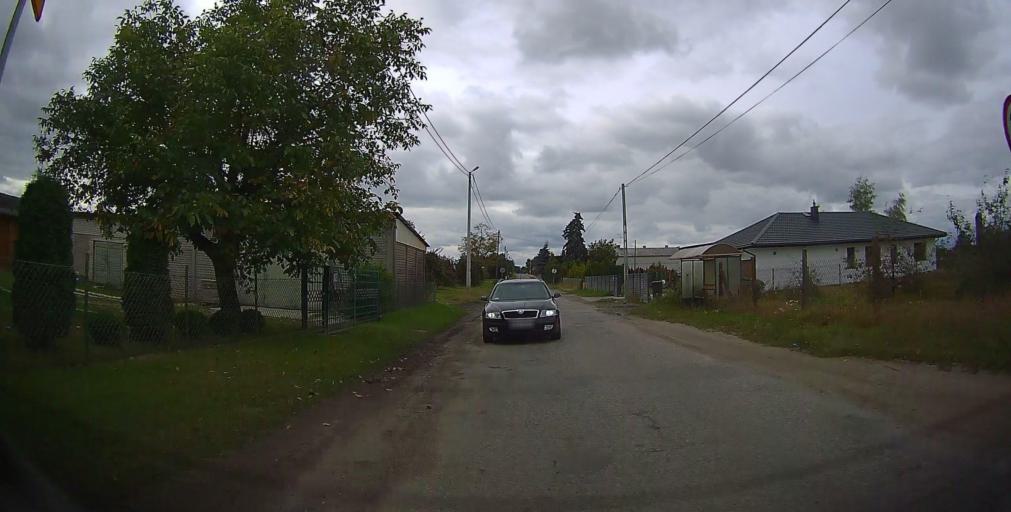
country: PL
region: Masovian Voivodeship
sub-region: Powiat grojecki
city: Belsk Duzy
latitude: 51.8152
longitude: 20.8290
